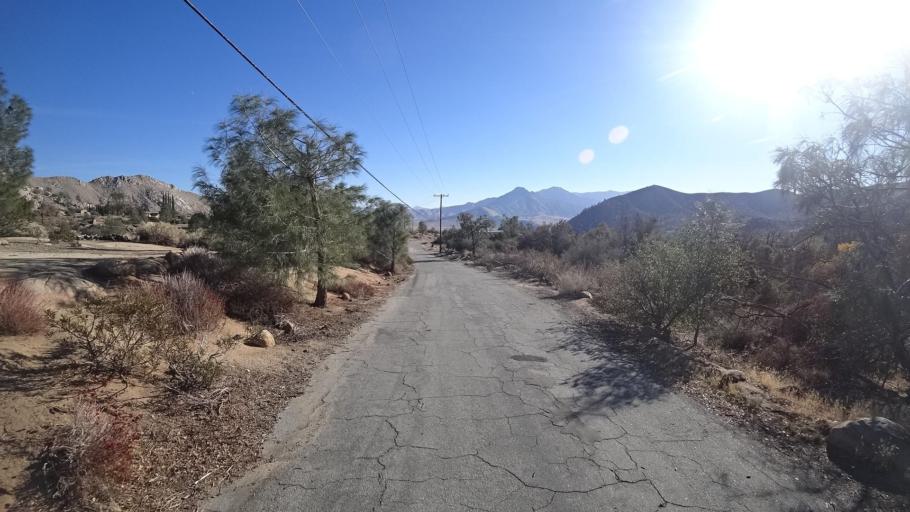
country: US
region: California
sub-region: Kern County
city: Weldon
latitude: 35.7141
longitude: -118.3054
